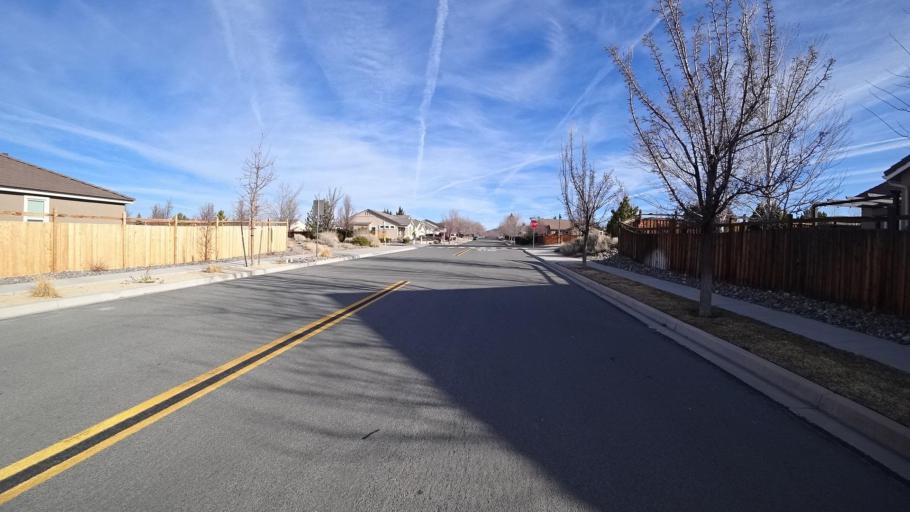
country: US
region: Nevada
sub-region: Washoe County
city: Spanish Springs
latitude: 39.6226
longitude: -119.6754
